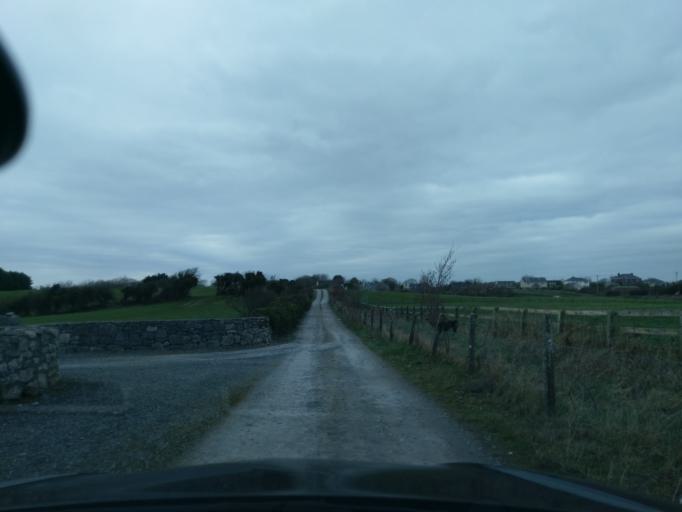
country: IE
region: Connaught
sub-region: County Galway
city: Oranmore
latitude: 53.2171
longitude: -8.8904
